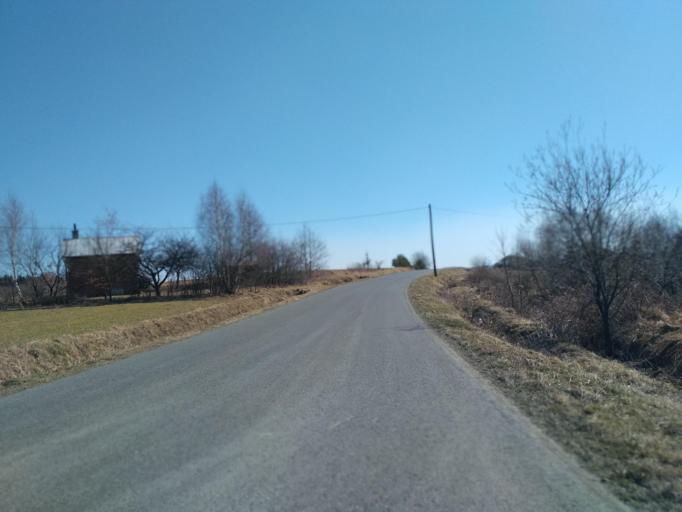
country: PL
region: Subcarpathian Voivodeship
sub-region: Powiat ropczycko-sedziszowski
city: Niedzwiada
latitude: 49.9638
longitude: 21.4744
